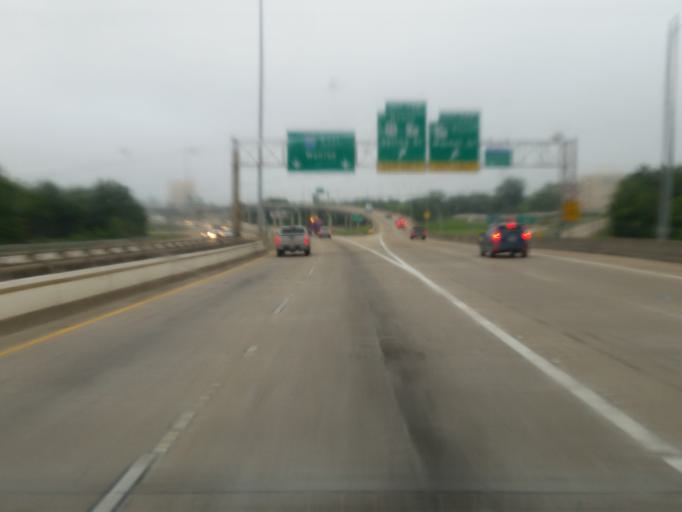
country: US
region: Louisiana
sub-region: Bossier Parish
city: Bossier City
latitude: 32.5018
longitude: -93.7495
